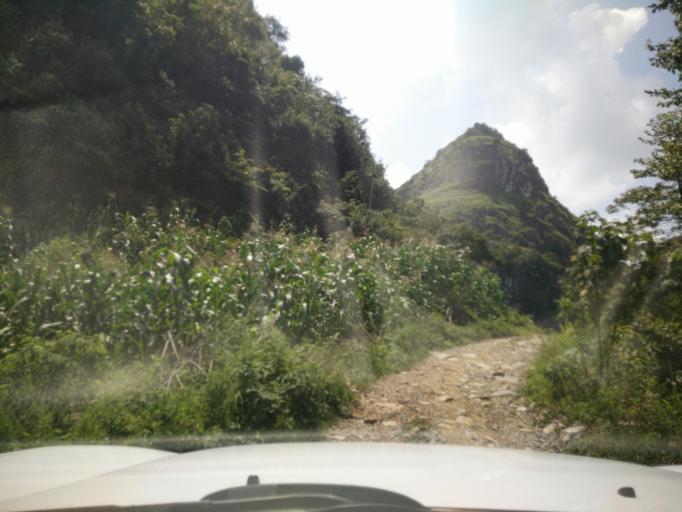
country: CN
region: Guangxi Zhuangzu Zizhiqu
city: Xinzhou
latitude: 25.0171
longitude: 105.7047
